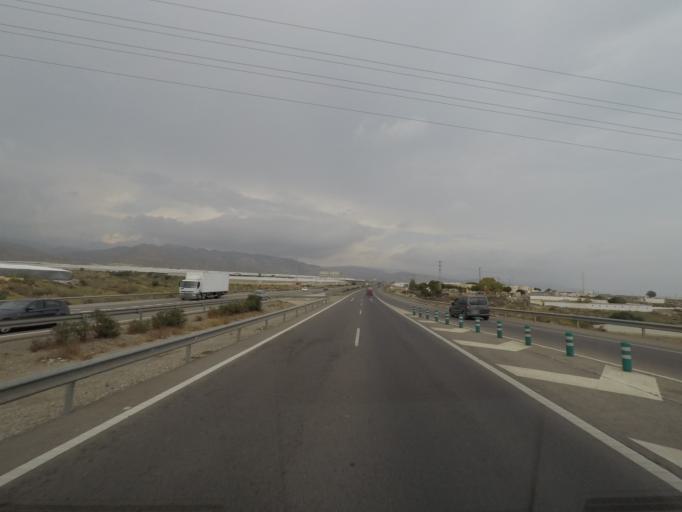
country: ES
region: Andalusia
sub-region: Provincia de Almeria
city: Vicar
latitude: 36.7966
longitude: -2.6841
